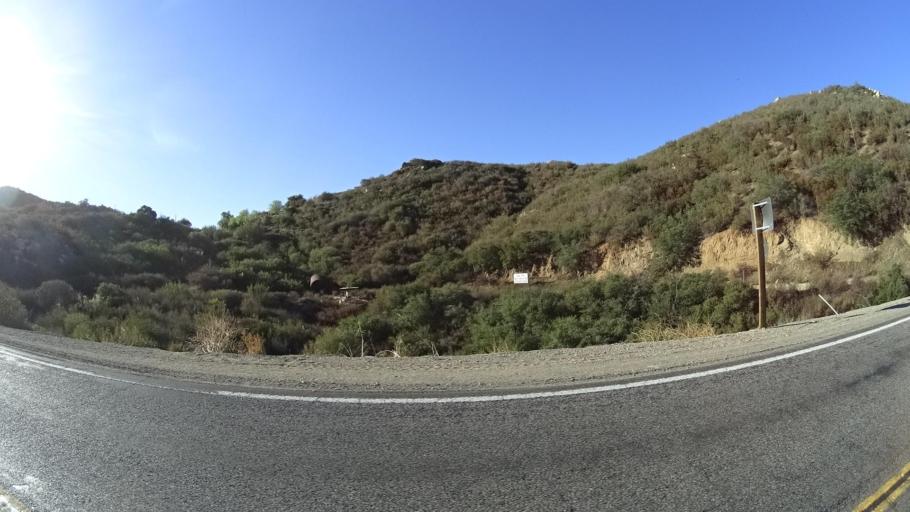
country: MX
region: Baja California
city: Tecate
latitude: 32.6008
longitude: -116.6402
